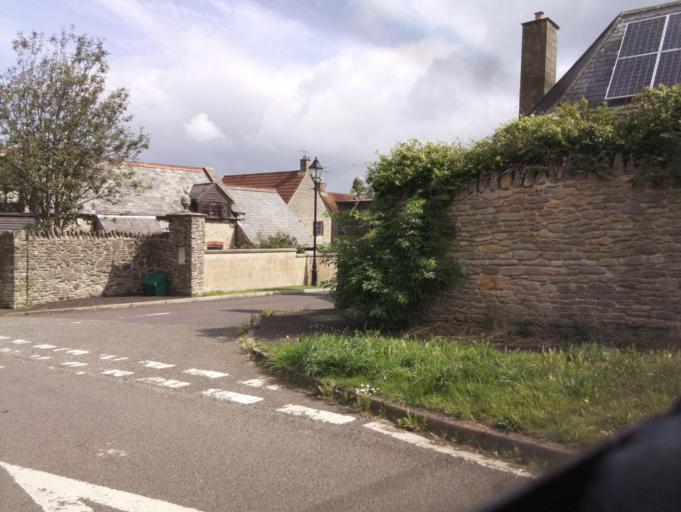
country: GB
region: England
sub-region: Somerset
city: Wincanton
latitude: 51.0038
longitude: -2.4187
